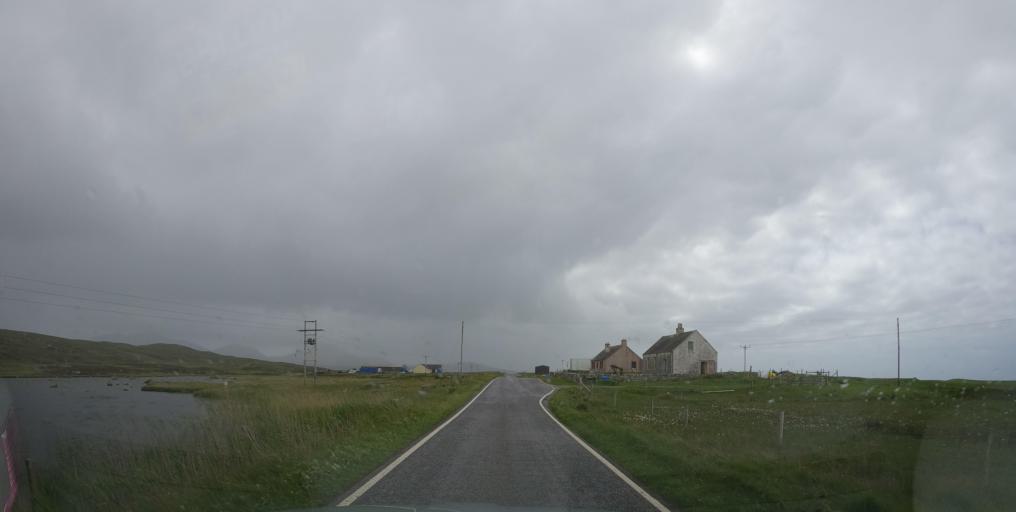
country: GB
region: Scotland
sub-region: Eilean Siar
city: Isle of South Uist
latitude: 57.3387
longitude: -7.3637
